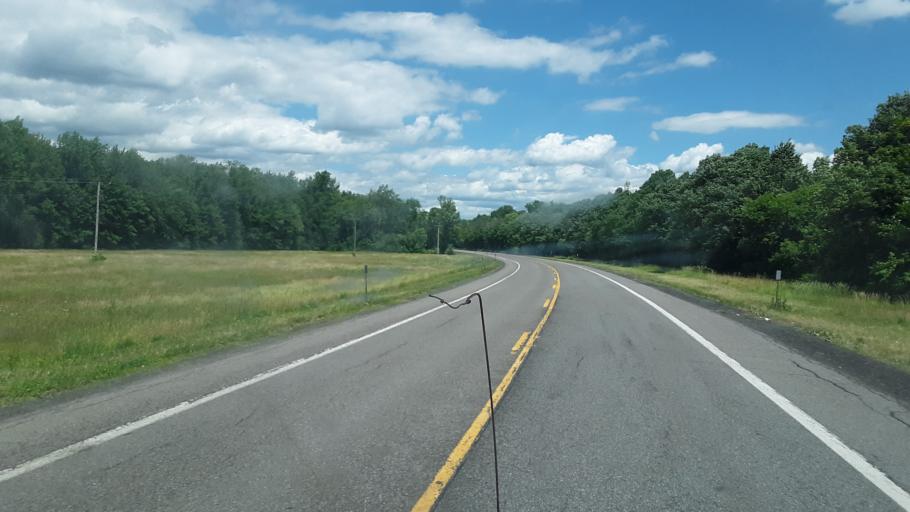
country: US
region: New York
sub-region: Madison County
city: Oneida
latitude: 43.1866
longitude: -75.6288
